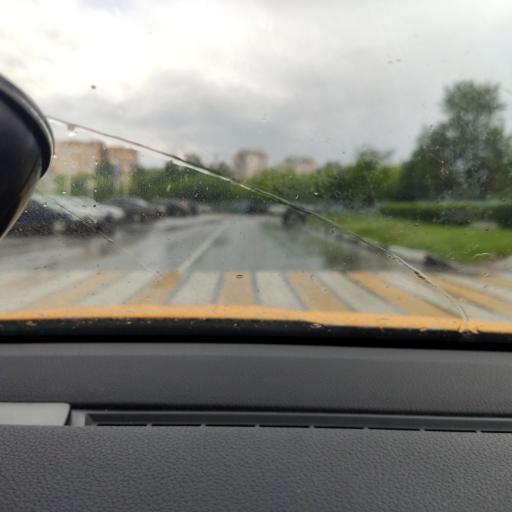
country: RU
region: Moskovskaya
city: Stupino
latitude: 54.8916
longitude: 38.0687
